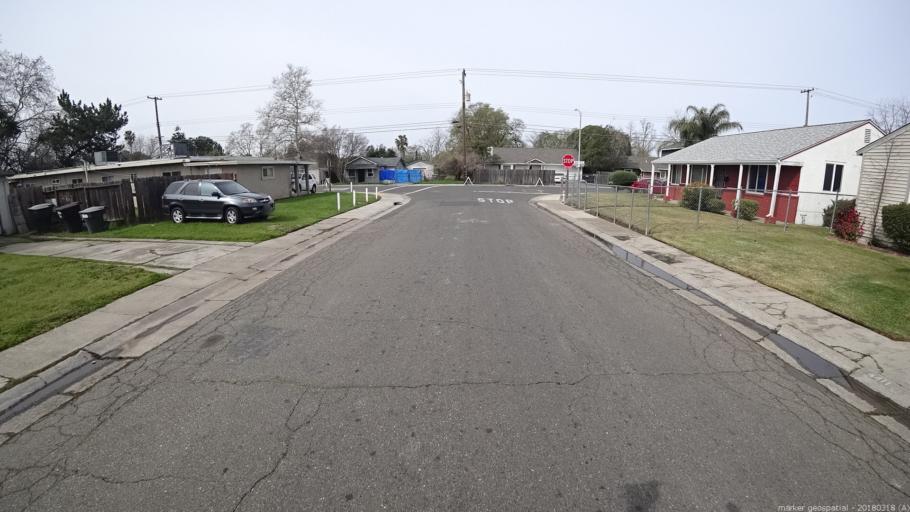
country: US
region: California
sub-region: Sacramento County
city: Parkway
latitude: 38.5375
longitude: -121.4551
